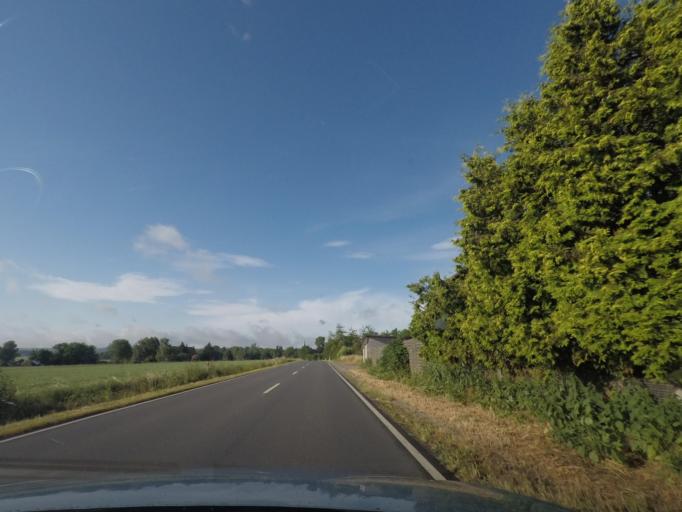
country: DE
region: Saxony-Anhalt
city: Huy-Neinstedt
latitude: 51.9926
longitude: 10.8936
